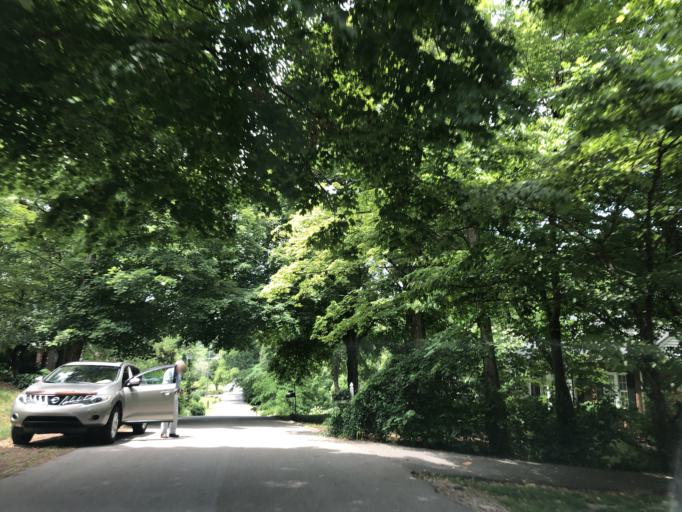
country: US
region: Tennessee
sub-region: Davidson County
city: Oak Hill
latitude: 36.1011
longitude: -86.7945
